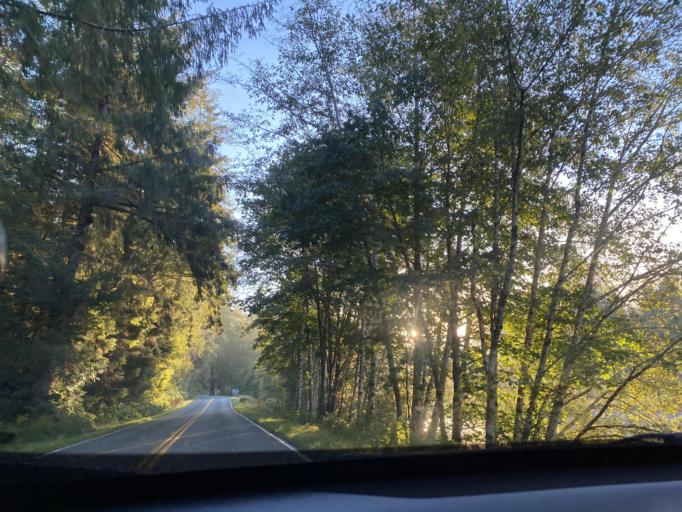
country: US
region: Washington
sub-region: Clallam County
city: Forks
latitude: 47.8226
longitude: -124.1933
